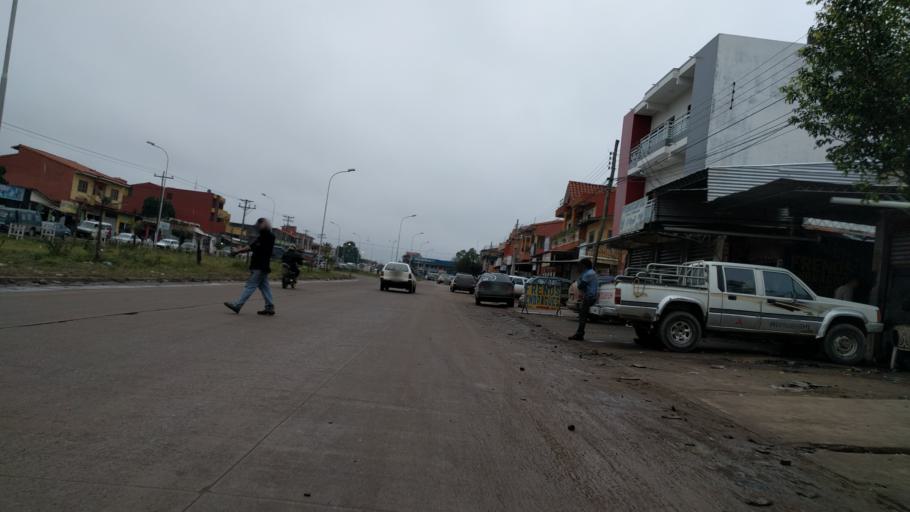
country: BO
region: Santa Cruz
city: Santa Cruz de la Sierra
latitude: -17.8290
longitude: -63.2009
